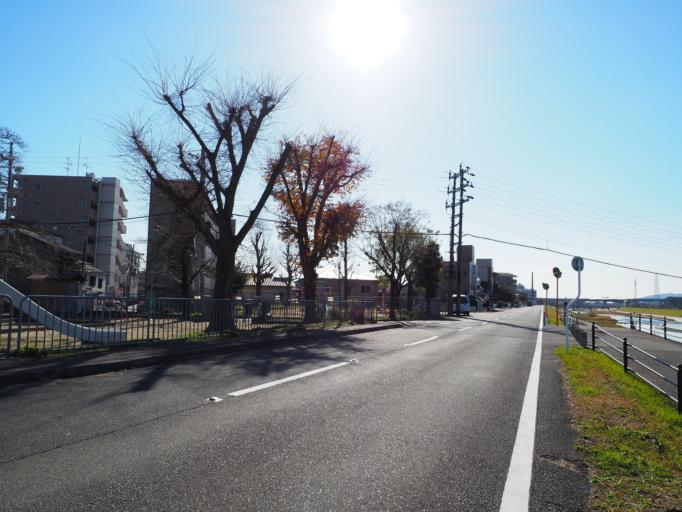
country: JP
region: Kyoto
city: Kyoto
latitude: 34.9692
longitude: 135.7621
